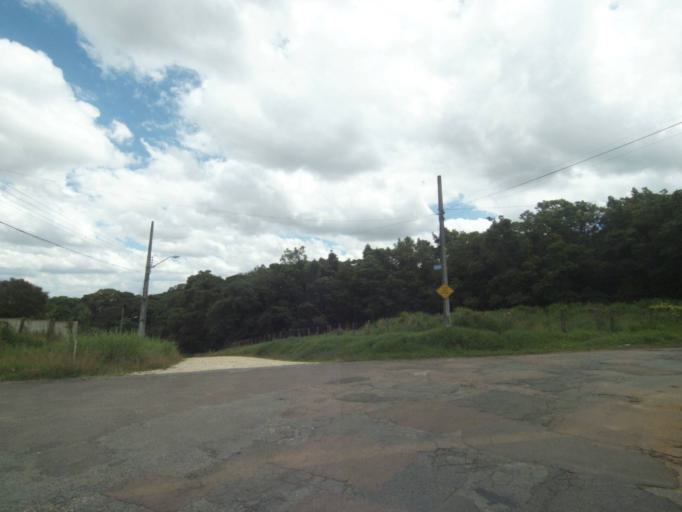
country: BR
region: Parana
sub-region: Curitiba
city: Curitiba
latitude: -25.4325
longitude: -49.3202
